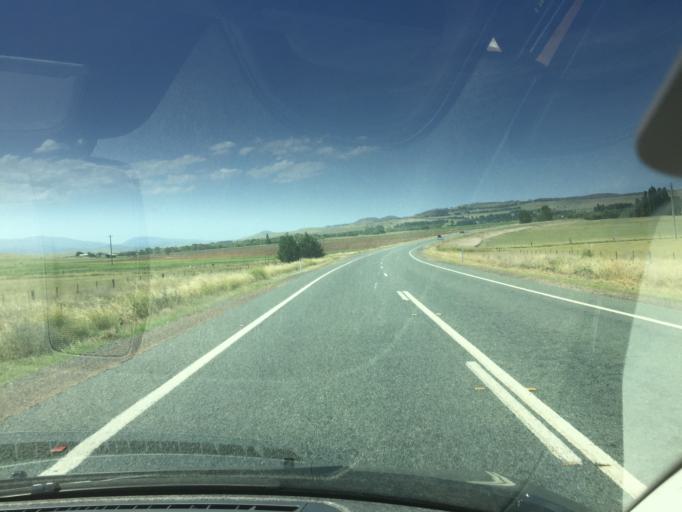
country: AU
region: New South Wales
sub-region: Cooma-Monaro
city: Cooma
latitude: -36.0907
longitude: 149.1453
